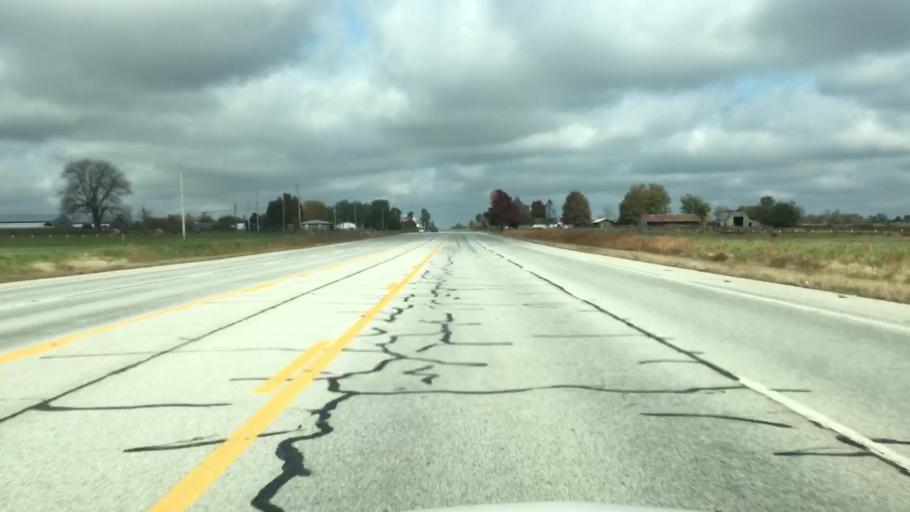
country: US
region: Arkansas
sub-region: Benton County
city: Siloam Springs
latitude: 36.2153
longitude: -94.4955
